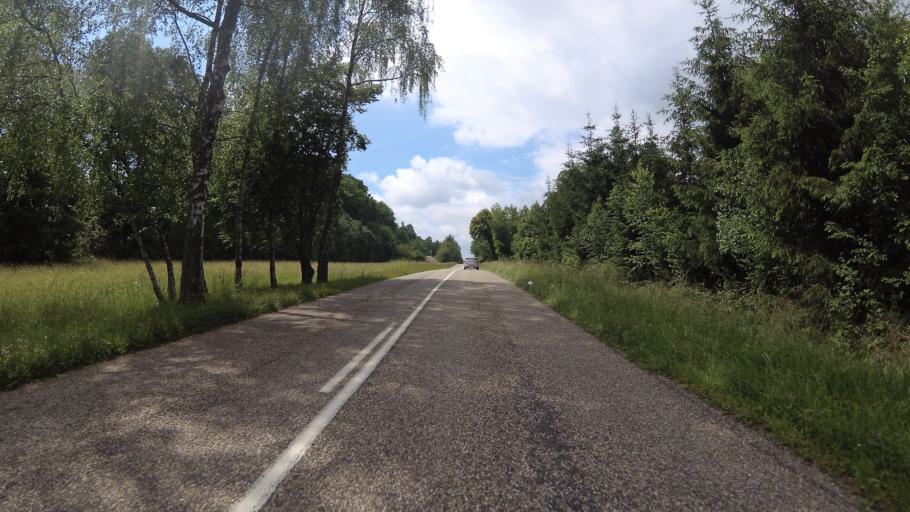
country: FR
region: Alsace
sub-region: Departement du Bas-Rhin
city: Herbitzheim
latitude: 49.0348
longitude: 7.0842
